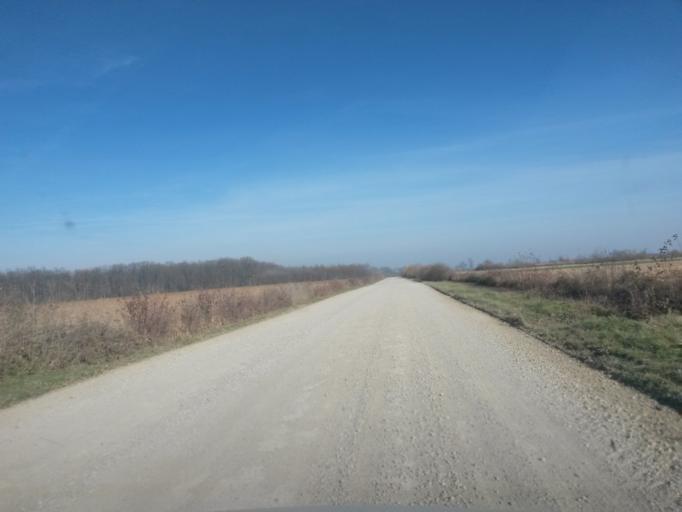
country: HR
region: Vukovarsko-Srijemska
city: Privlaka
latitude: 45.2239
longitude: 18.8743
